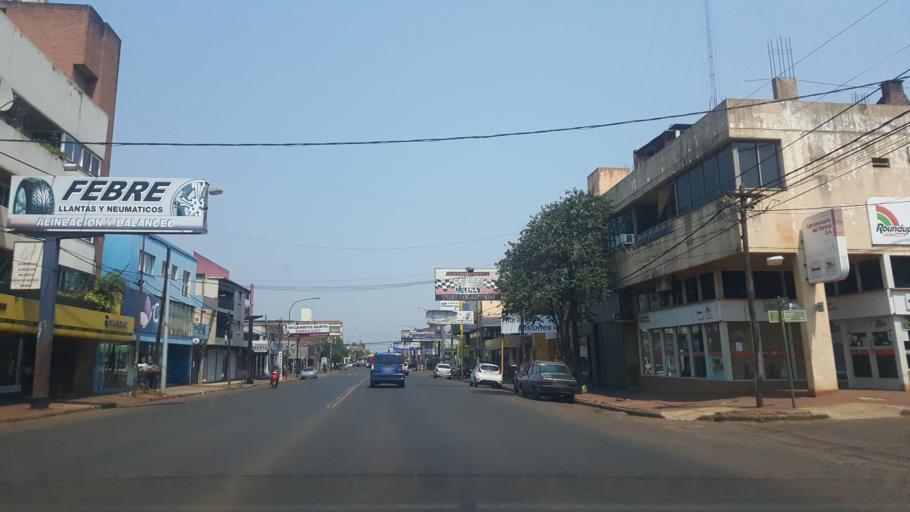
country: AR
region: Misiones
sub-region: Departamento de Capital
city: Posadas
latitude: -27.3932
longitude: -55.9012
